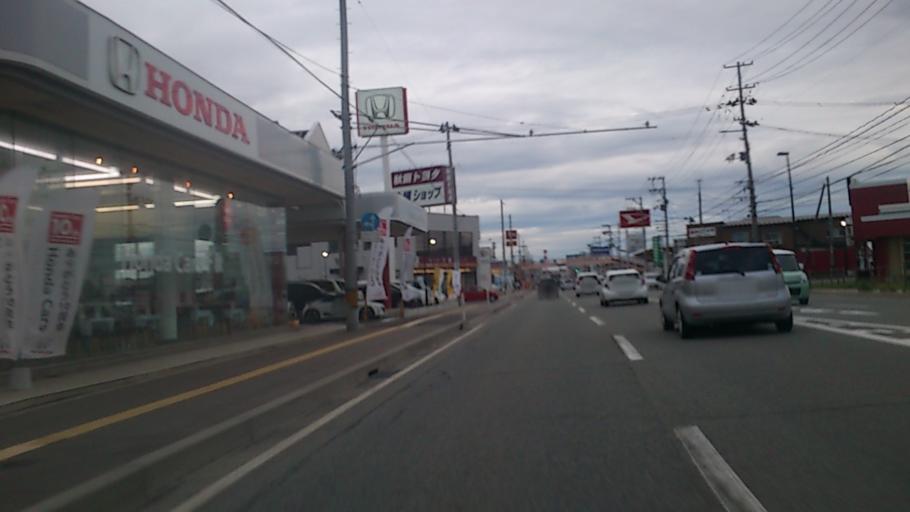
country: JP
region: Akita
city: Akita Shi
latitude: 39.7336
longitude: 140.1007
